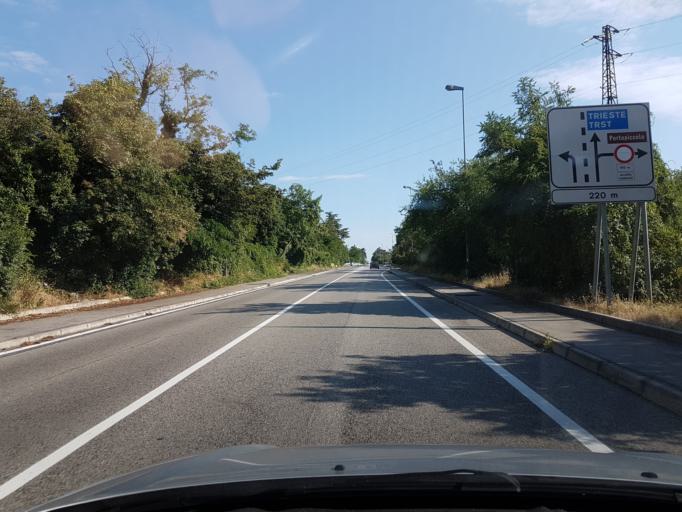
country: IT
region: Friuli Venezia Giulia
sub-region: Provincia di Trieste
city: Sistiana-Visogliano
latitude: 45.7686
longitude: 13.6392
